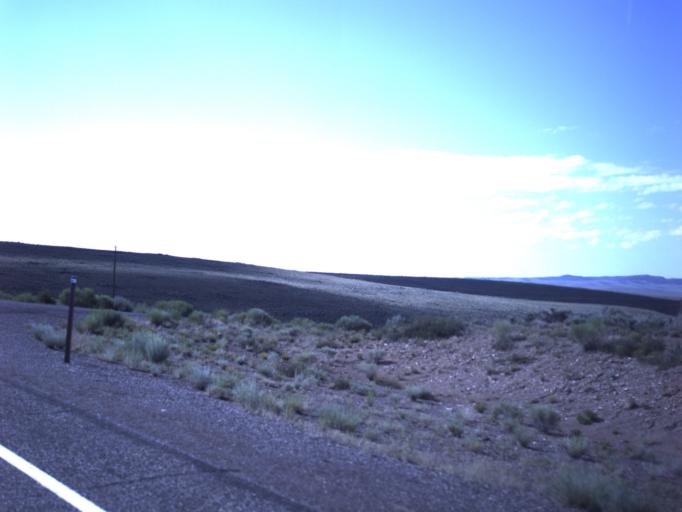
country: US
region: Utah
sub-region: Wayne County
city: Loa
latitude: 38.4533
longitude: -111.8311
